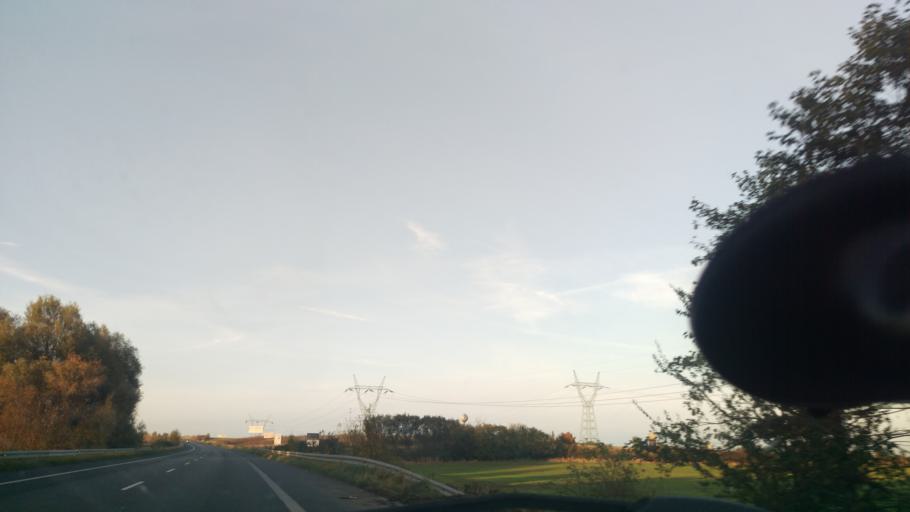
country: PL
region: West Pomeranian Voivodeship
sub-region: Powiat gryfinski
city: Stare Czarnowo
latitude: 53.2854
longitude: 14.7870
